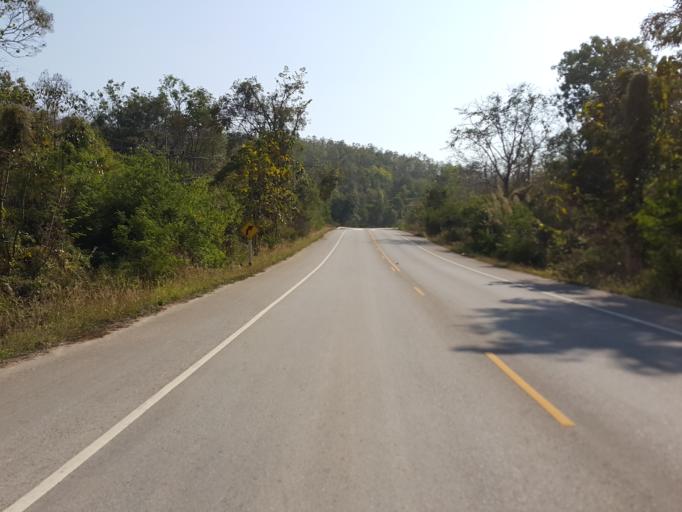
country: TH
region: Lampang
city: Chae Hom
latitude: 18.7827
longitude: 99.5845
